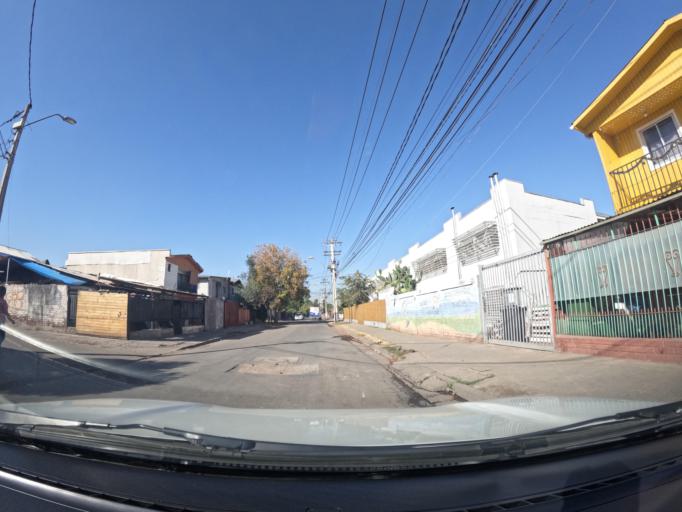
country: CL
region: Santiago Metropolitan
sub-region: Provincia de Santiago
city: Villa Presidente Frei, Nunoa, Santiago, Chile
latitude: -33.4771
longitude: -70.5738
